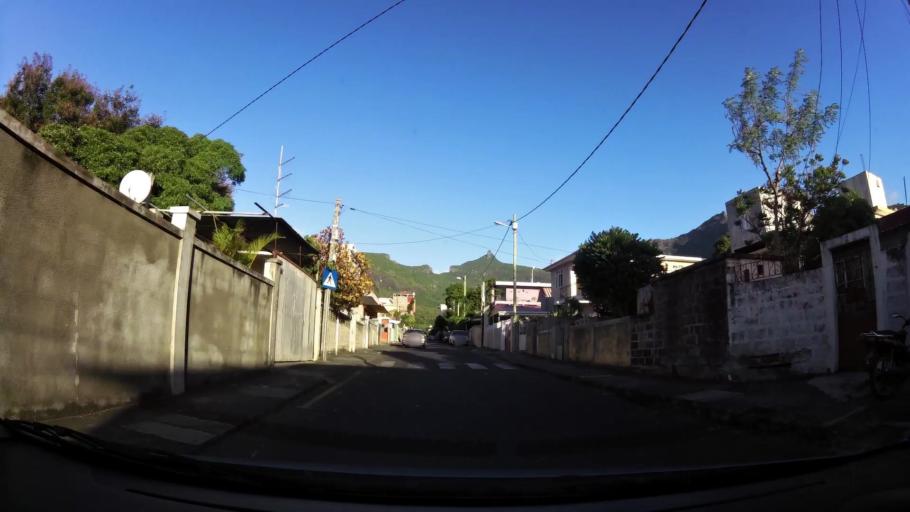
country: MU
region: Port Louis
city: Port Louis
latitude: -20.1729
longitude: 57.5104
